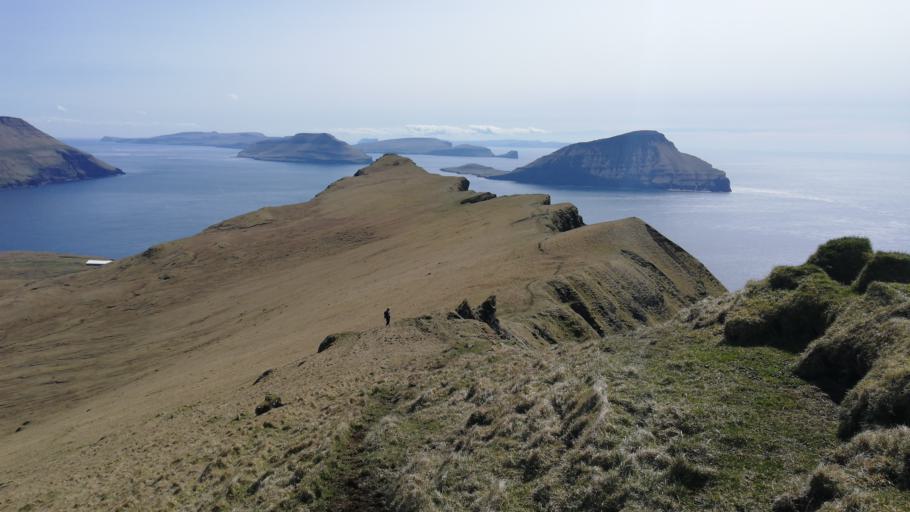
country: FO
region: Streymoy
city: Kollafjordhur
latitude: 62.0508
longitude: -6.9867
